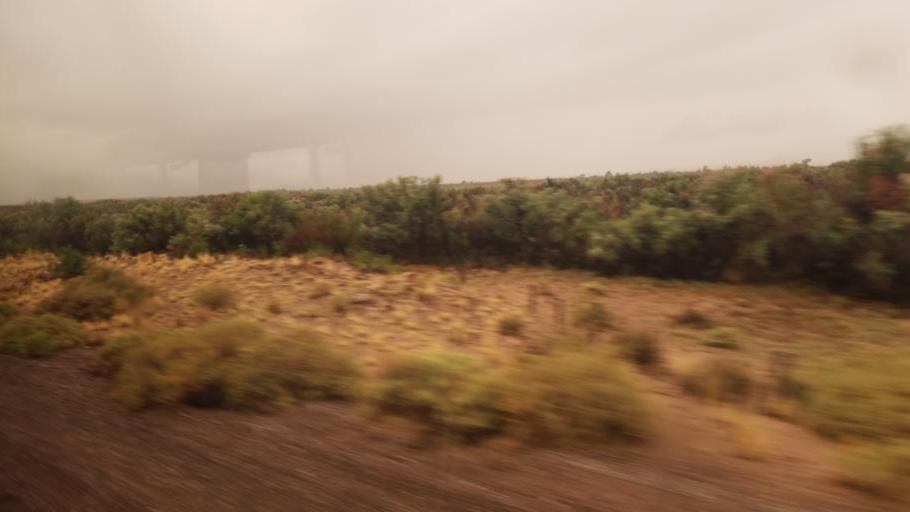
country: US
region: Arizona
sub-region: Navajo County
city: Joseph City
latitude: 34.9674
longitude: -110.4591
